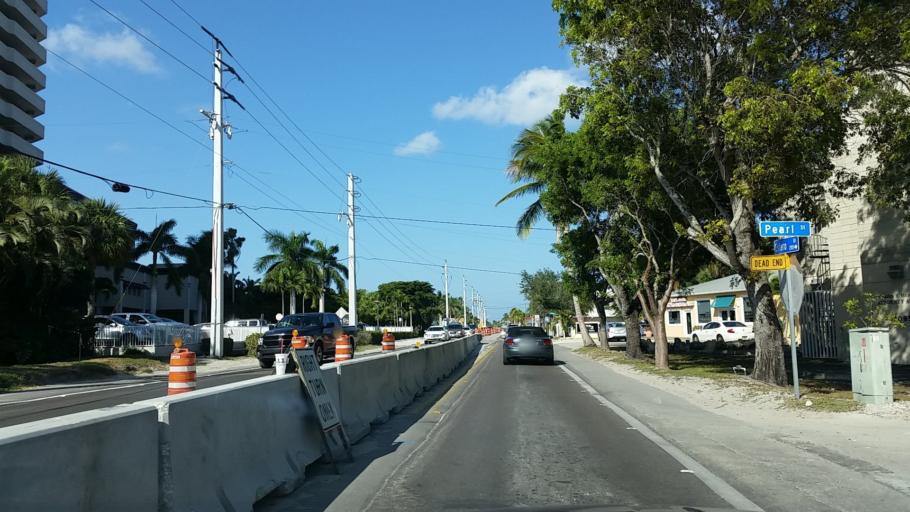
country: US
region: Florida
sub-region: Lee County
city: Fort Myers Beach
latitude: 26.4499
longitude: -81.9461
